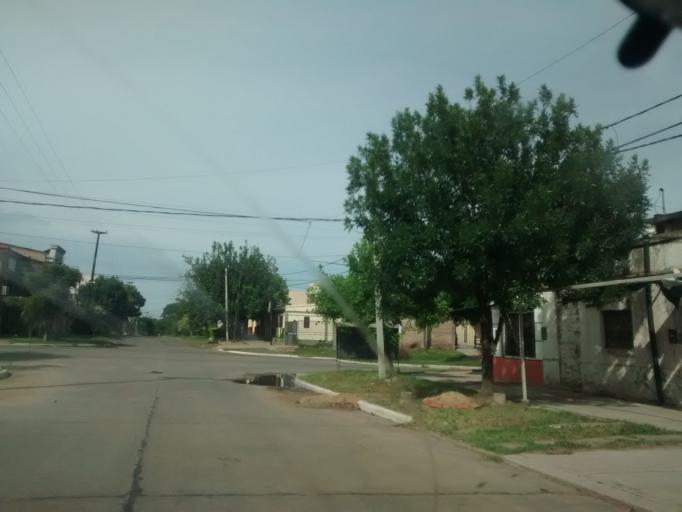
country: AR
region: Chaco
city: Resistencia
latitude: -27.4379
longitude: -58.9933
